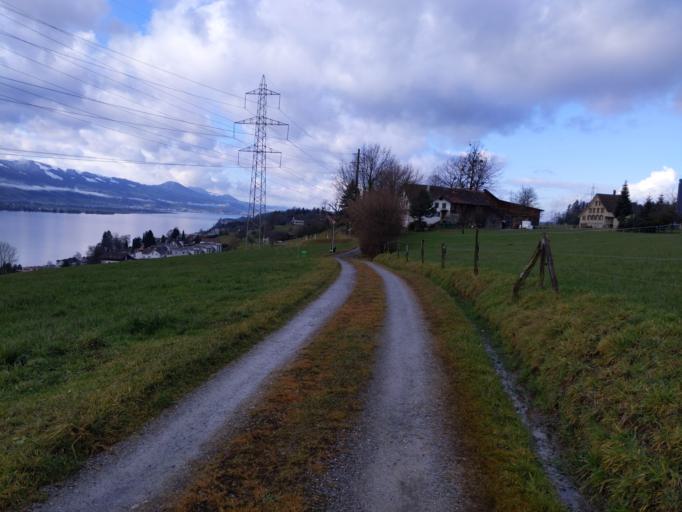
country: CH
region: Saint Gallen
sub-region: Wahlkreis See-Gaster
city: Schmerikon
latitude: 47.2303
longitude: 8.9434
